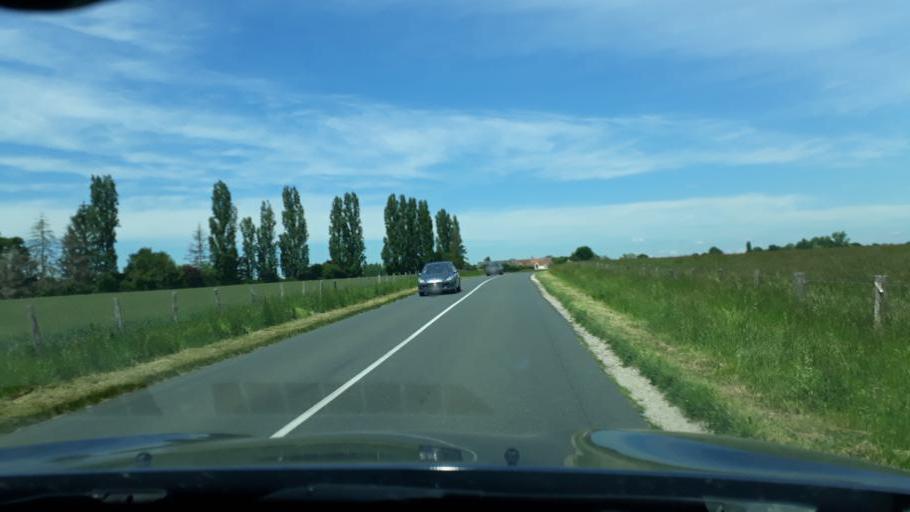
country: FR
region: Centre
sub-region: Departement du Loiret
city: Boiscommun
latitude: 48.0490
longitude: 2.2993
